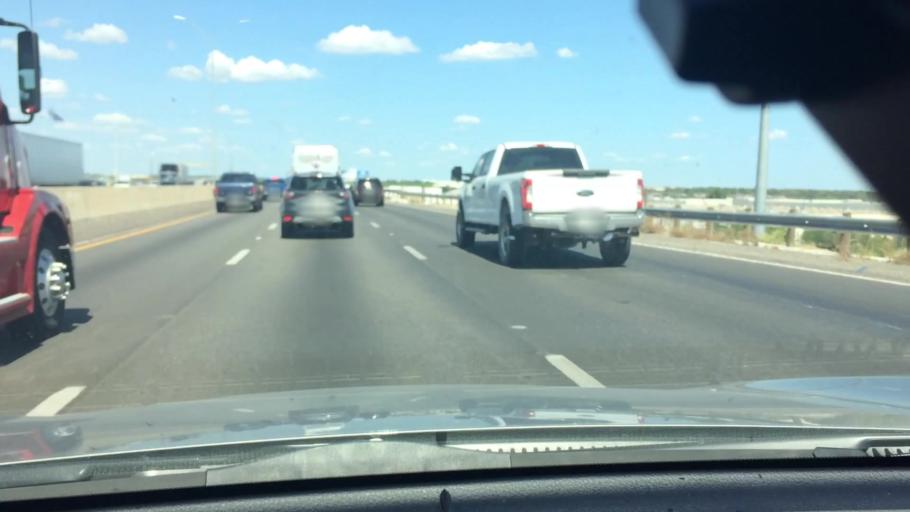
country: US
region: Texas
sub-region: Bexar County
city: Terrell Hills
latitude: 29.4400
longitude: -98.4438
